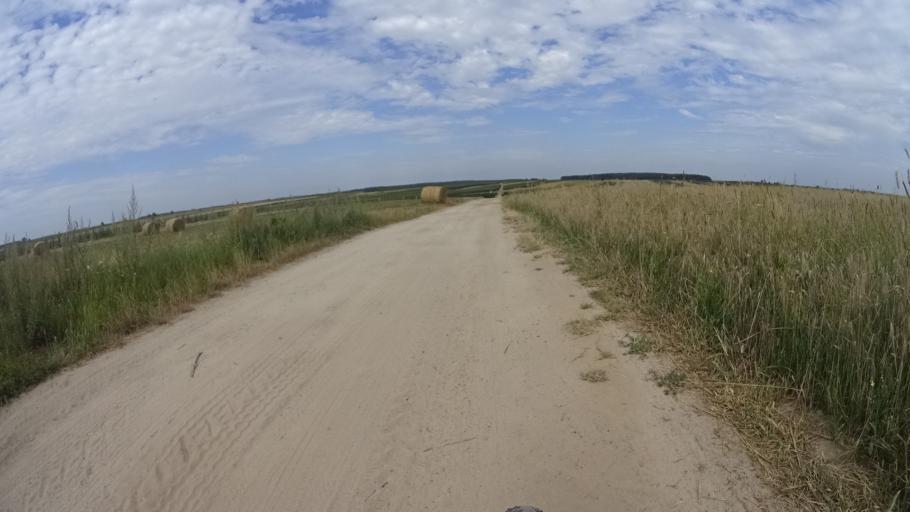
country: PL
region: Masovian Voivodeship
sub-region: Powiat bialobrzeski
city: Wysmierzyce
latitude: 51.6567
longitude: 20.8023
